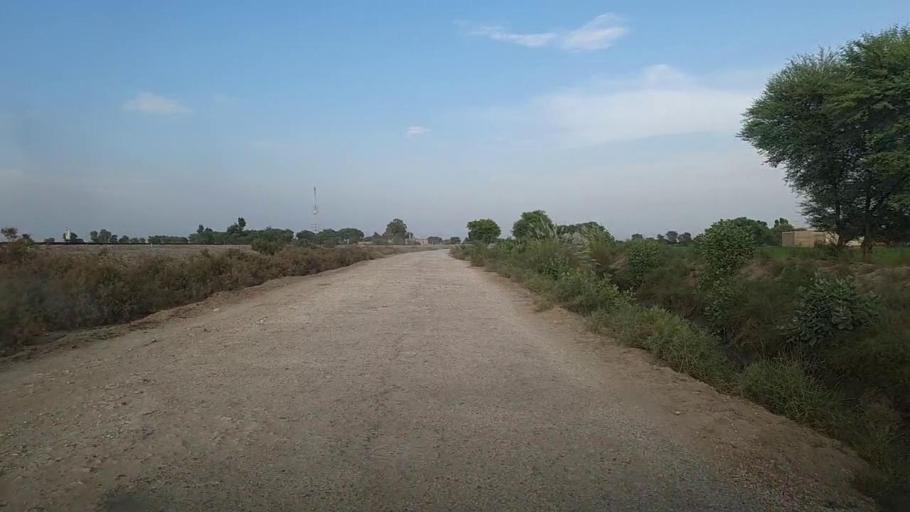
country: PK
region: Sindh
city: Tangwani
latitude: 28.2973
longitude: 68.8852
